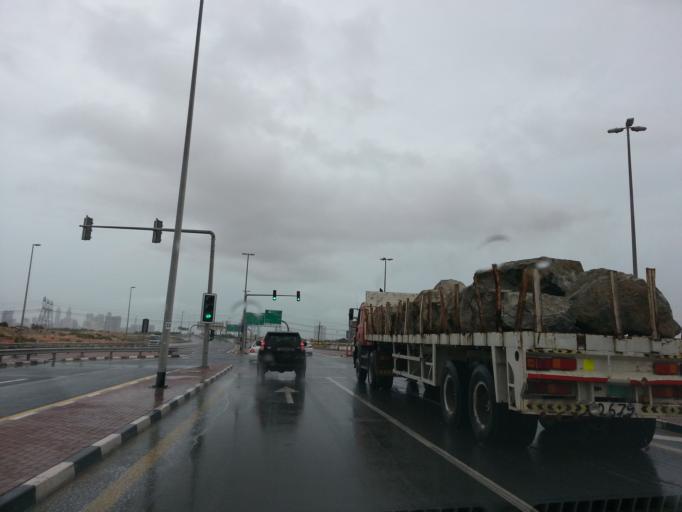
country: AE
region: Dubai
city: Dubai
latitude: 25.0708
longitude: 55.2171
